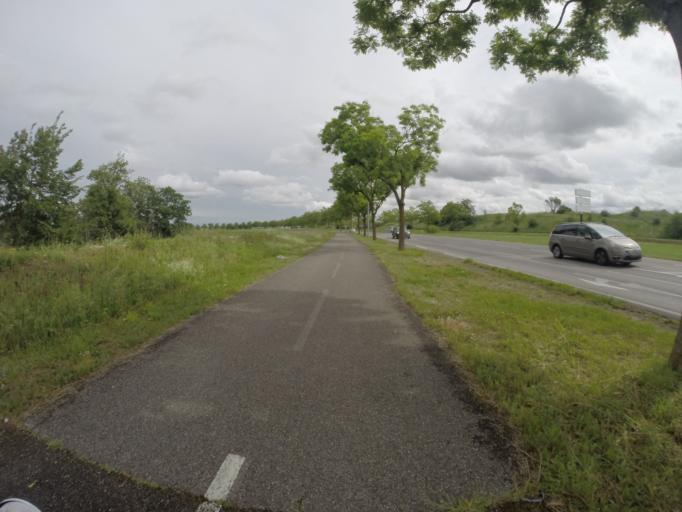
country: FR
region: Rhone-Alpes
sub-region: Departement du Rhone
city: Bron
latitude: 45.7393
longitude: 4.9356
